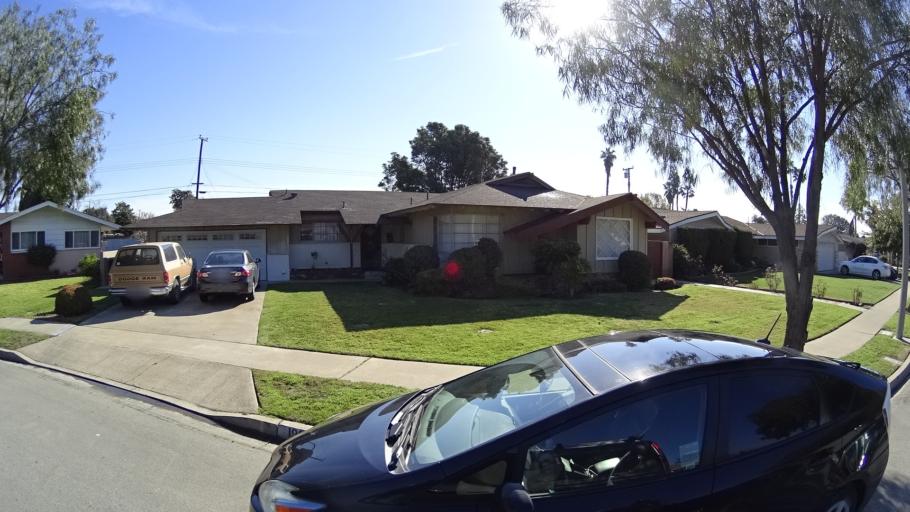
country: US
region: California
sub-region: Orange County
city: Garden Grove
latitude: 33.8002
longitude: -117.9259
